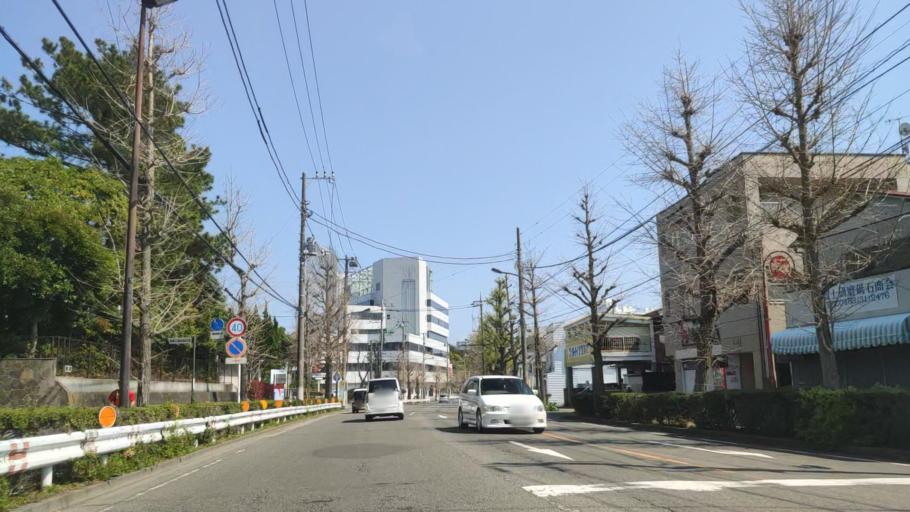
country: JP
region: Kanagawa
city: Hiratsuka
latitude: 35.3352
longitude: 139.3441
